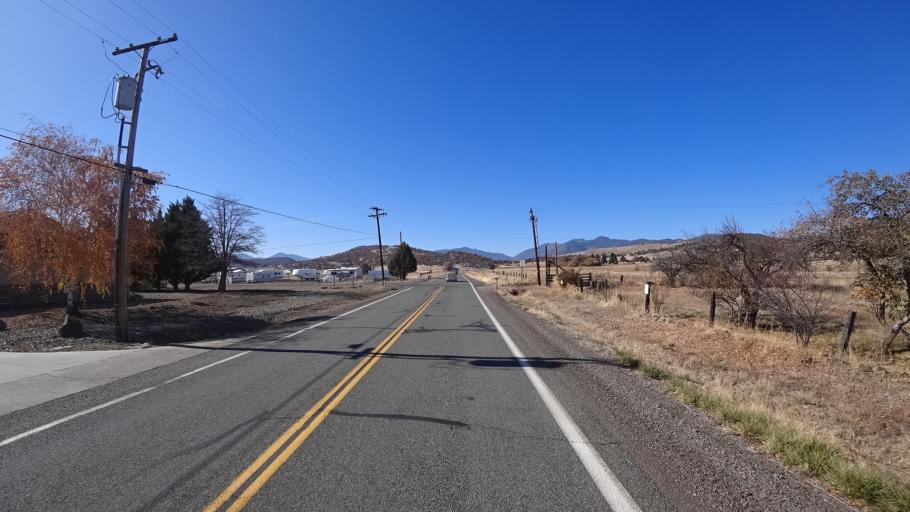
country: US
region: California
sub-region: Siskiyou County
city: Yreka
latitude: 41.7426
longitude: -122.5927
